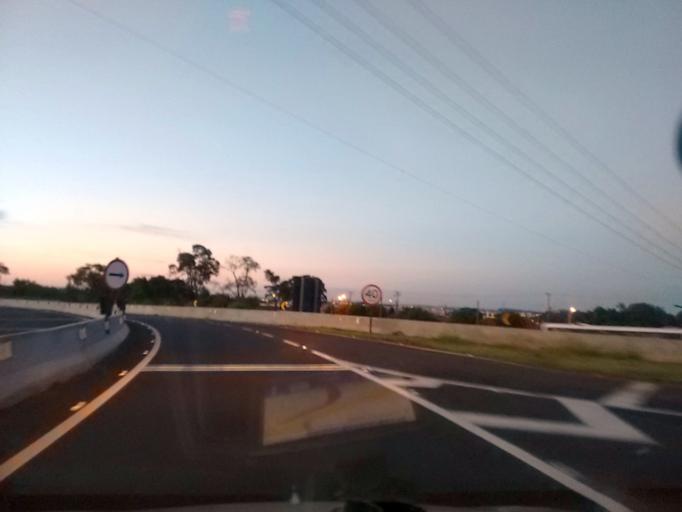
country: BR
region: Sao Paulo
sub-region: Araraquara
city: Araraquara
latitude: -21.8067
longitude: -48.1956
